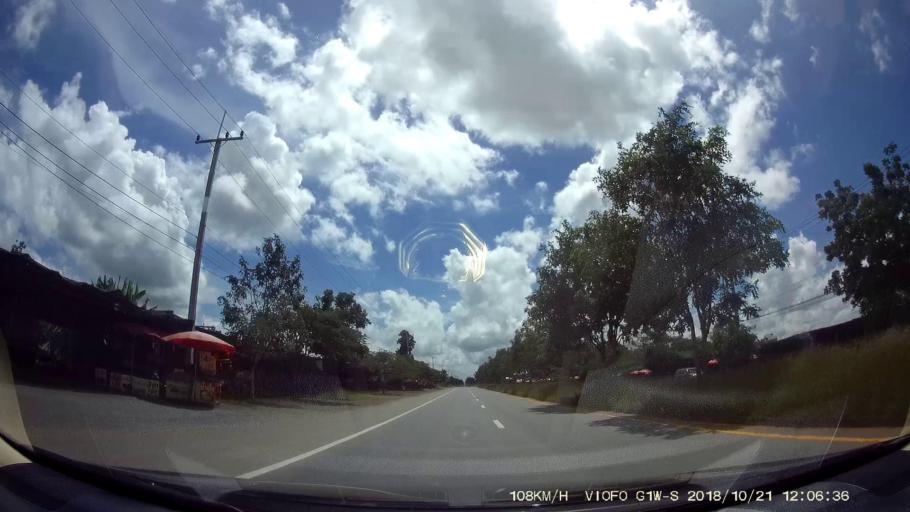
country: TH
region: Chaiyaphum
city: Chatturat
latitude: 15.4603
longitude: 101.8264
